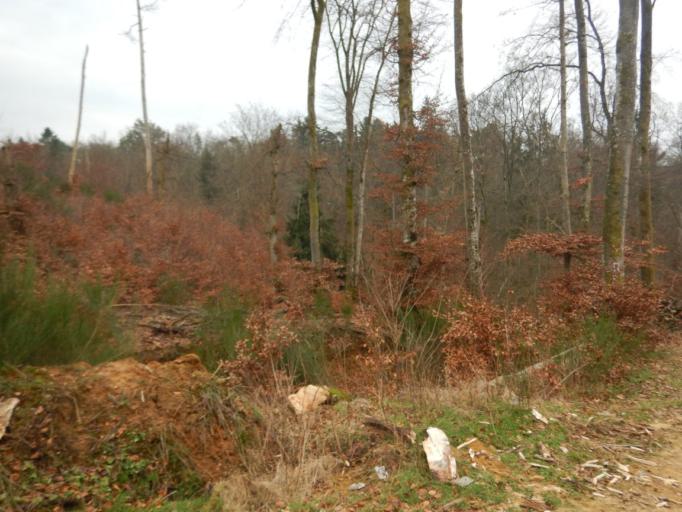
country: LU
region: Luxembourg
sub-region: Canton de Capellen
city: Koerich
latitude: 49.6782
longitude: 5.9505
